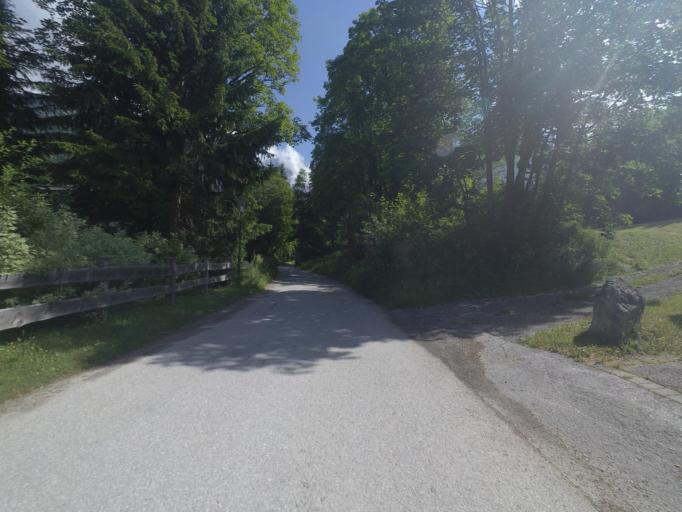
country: AT
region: Salzburg
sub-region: Politischer Bezirk Zell am See
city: Dienten am Hochkonig
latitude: 47.4133
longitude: 12.9811
